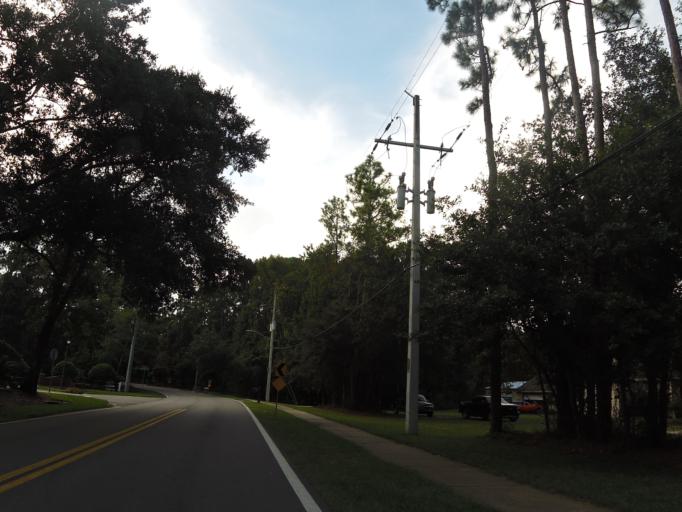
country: US
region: Florida
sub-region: Saint Johns County
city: Fruit Cove
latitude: 30.1405
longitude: -81.6121
